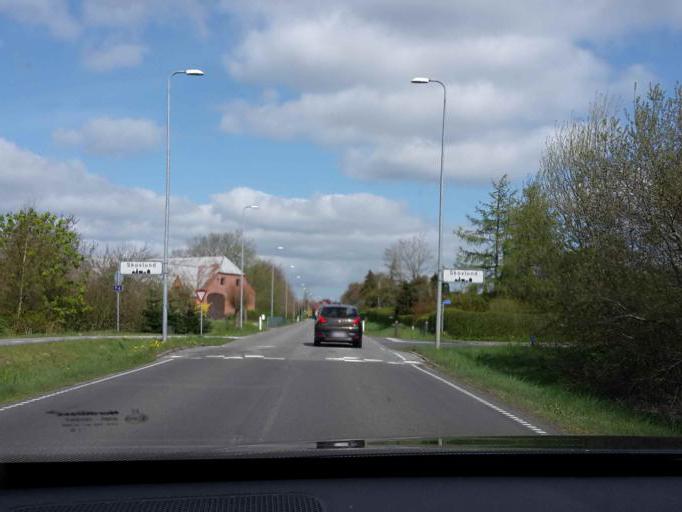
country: DK
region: South Denmark
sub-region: Varde Kommune
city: Olgod
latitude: 55.7333
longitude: 8.7122
